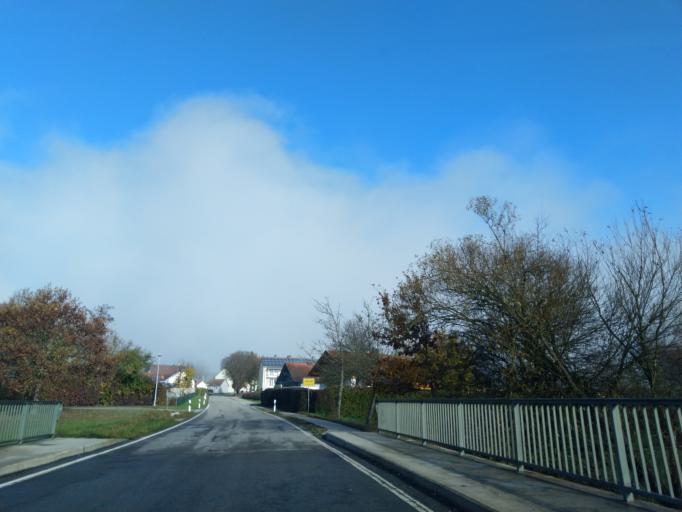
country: DE
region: Bavaria
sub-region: Lower Bavaria
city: Aussernzell
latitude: 48.7213
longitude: 13.2026
